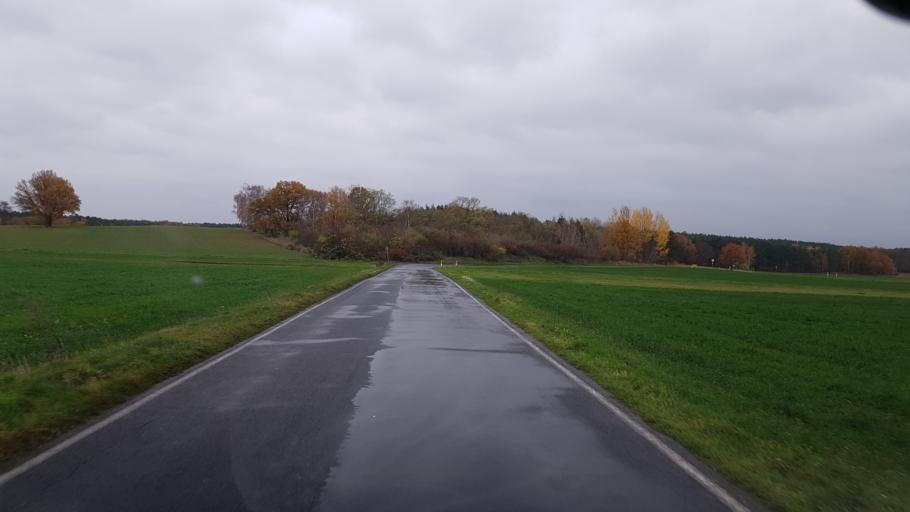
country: DE
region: Brandenburg
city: Ortrand
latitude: 51.3648
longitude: 13.7655
